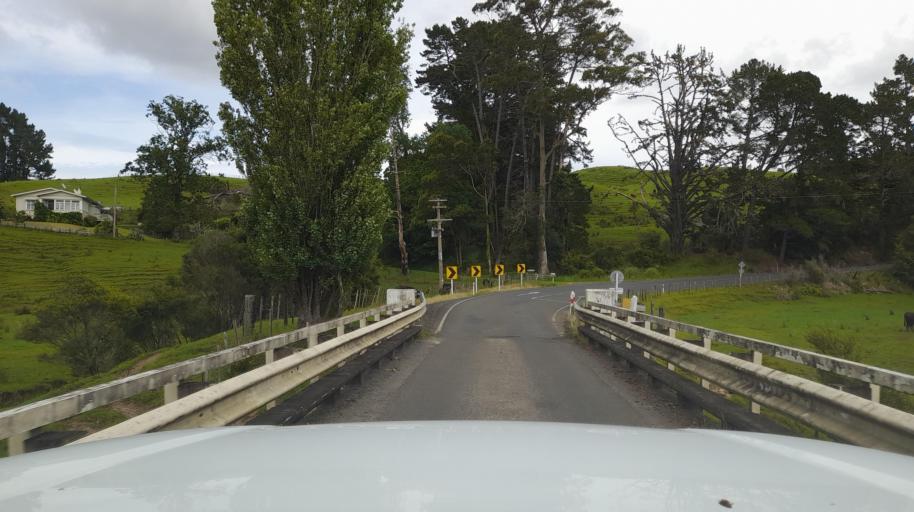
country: NZ
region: Northland
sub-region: Far North District
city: Ahipara
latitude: -35.2721
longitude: 173.2836
